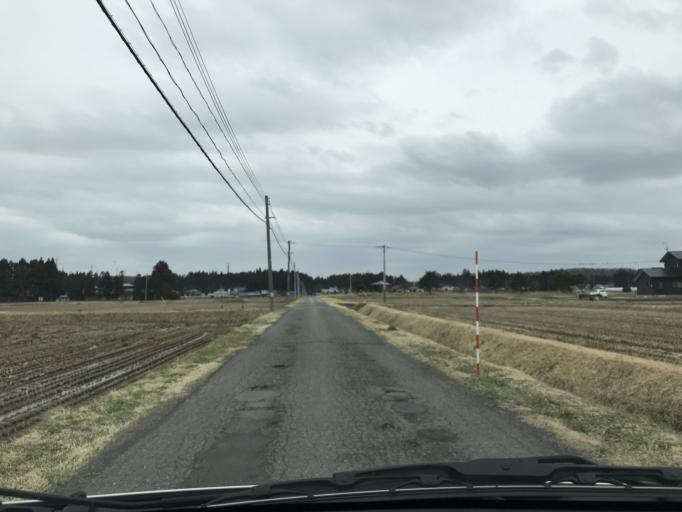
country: JP
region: Iwate
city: Kitakami
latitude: 39.2244
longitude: 141.0769
